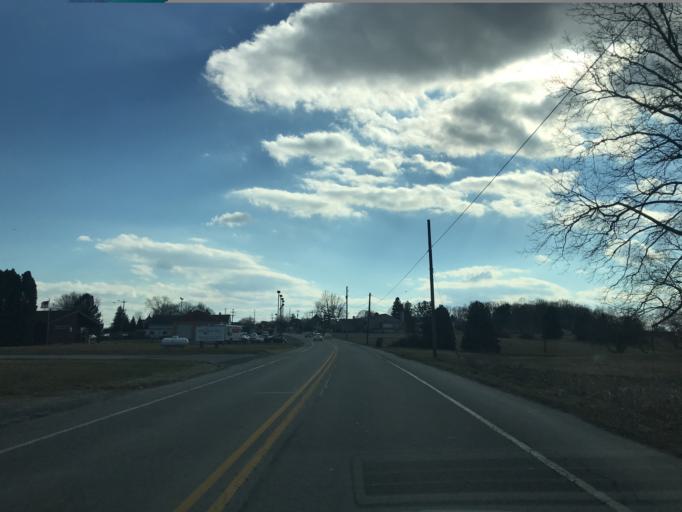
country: US
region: Pennsylvania
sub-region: Chester County
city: Oxford
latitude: 39.7522
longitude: -76.0165
